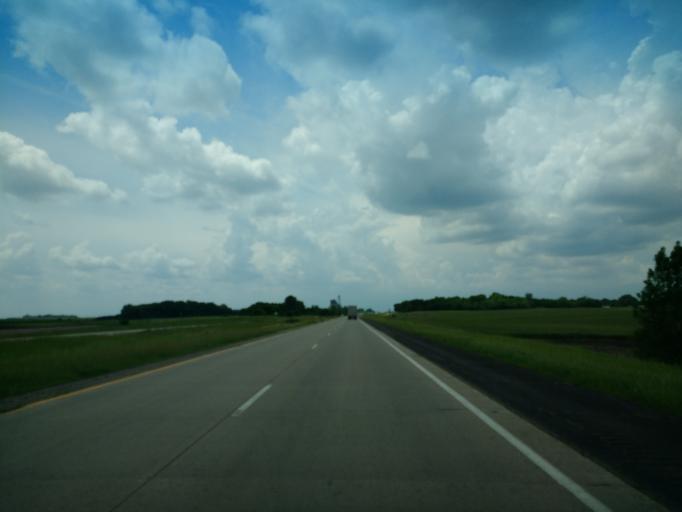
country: US
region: Minnesota
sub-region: Cottonwood County
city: Windom
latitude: 43.8283
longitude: -95.1841
